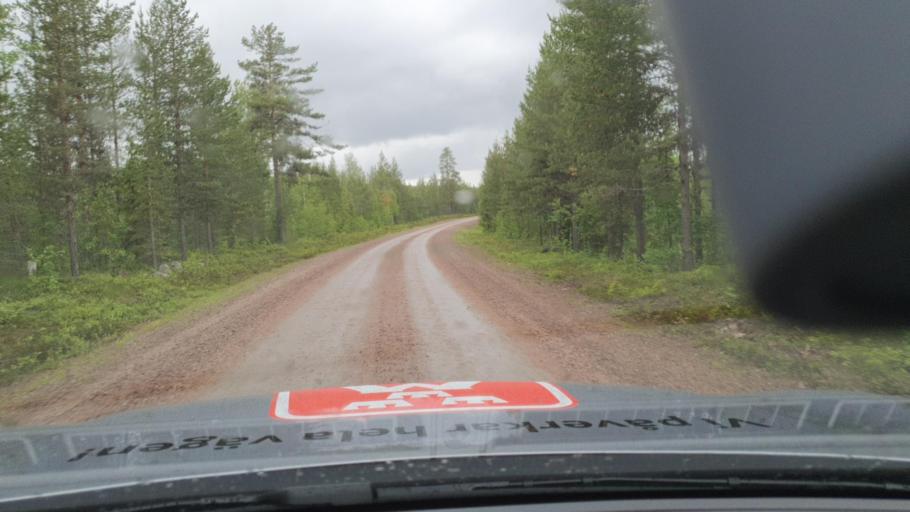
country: SE
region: Norrbotten
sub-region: Overkalix Kommun
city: OEverkalix
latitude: 66.6402
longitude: 22.7023
